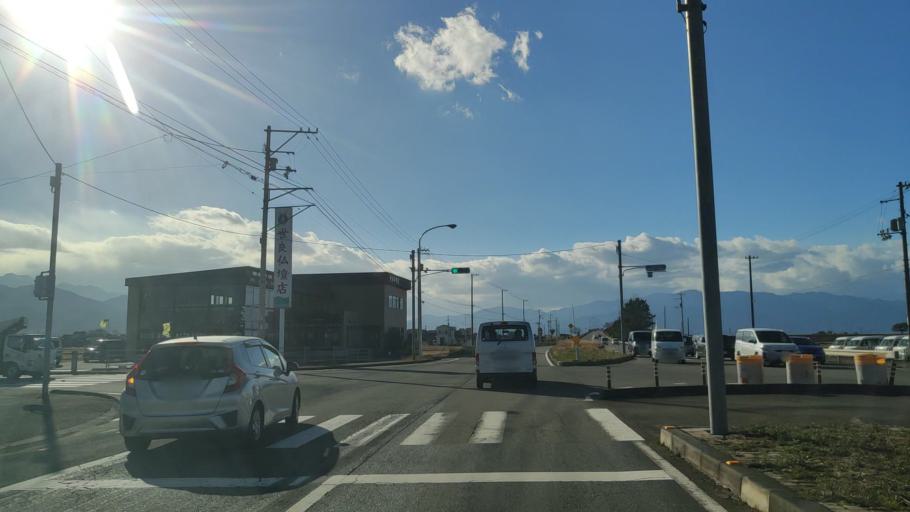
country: JP
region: Ehime
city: Saijo
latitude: 33.9193
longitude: 133.1615
